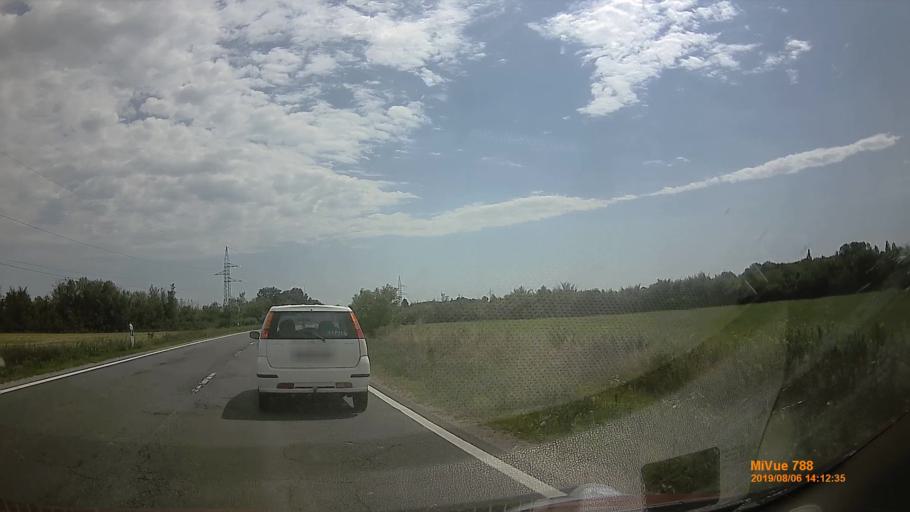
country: HU
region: Vas
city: Taplanszentkereszt
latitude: 47.2090
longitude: 16.6791
